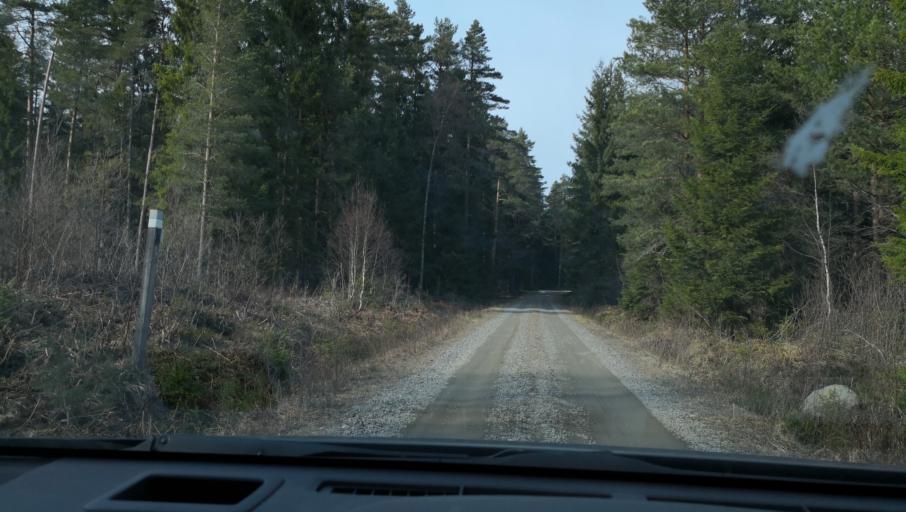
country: SE
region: OErebro
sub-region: Lindesbergs Kommun
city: Frovi
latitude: 59.3771
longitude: 15.4205
